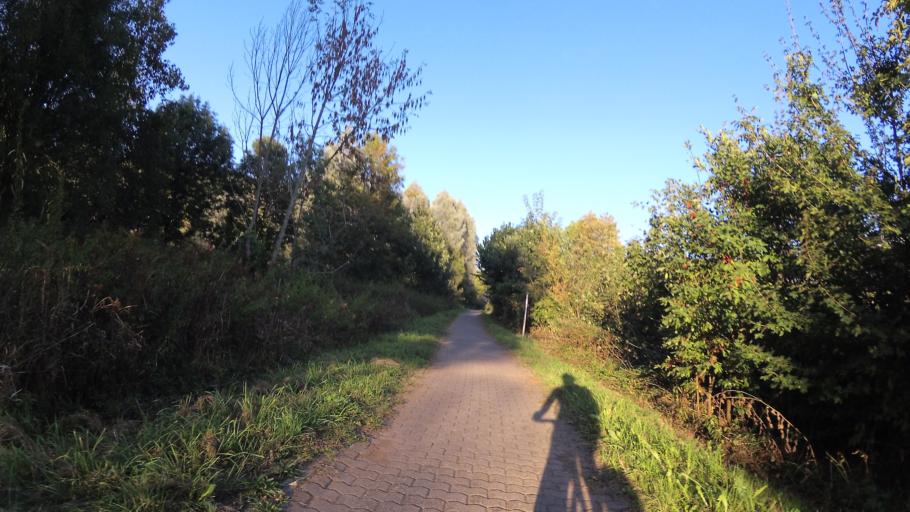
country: DE
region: Saarland
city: Eppelborn
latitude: 49.4125
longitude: 6.9784
